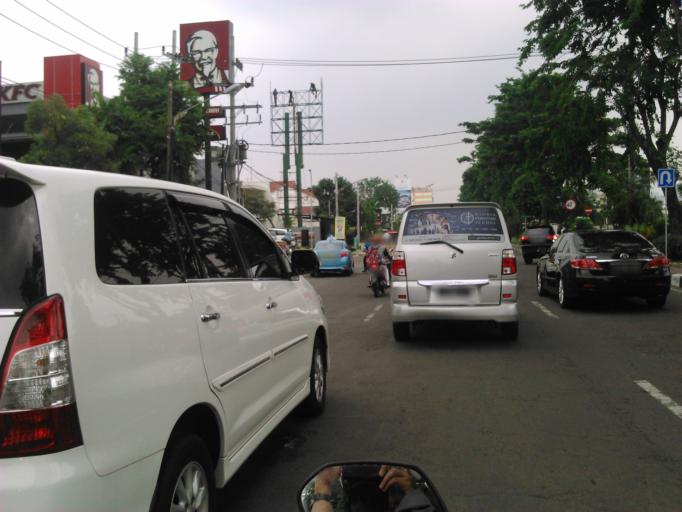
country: ID
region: East Java
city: Gubengairlangga
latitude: -7.2804
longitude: 112.7702
